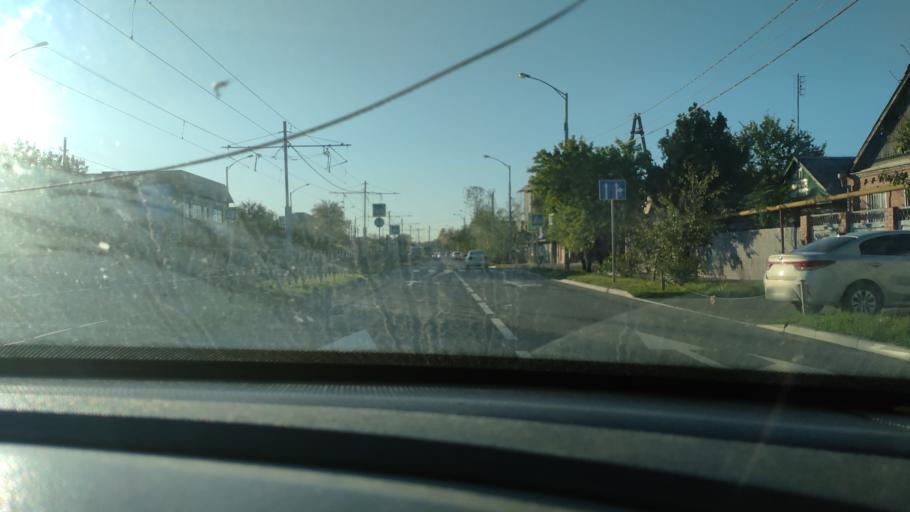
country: RU
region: Krasnodarskiy
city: Krasnodar
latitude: 45.0430
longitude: 38.9392
